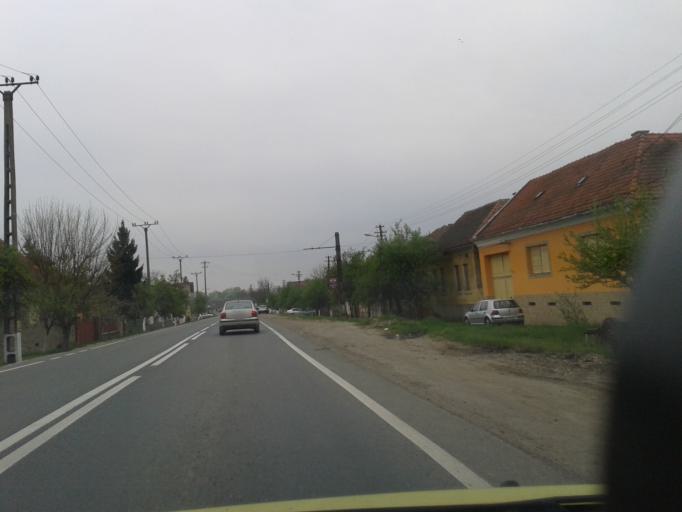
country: RO
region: Arad
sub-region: Oras Lipova
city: Radna
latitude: 46.0963
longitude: 21.6795
